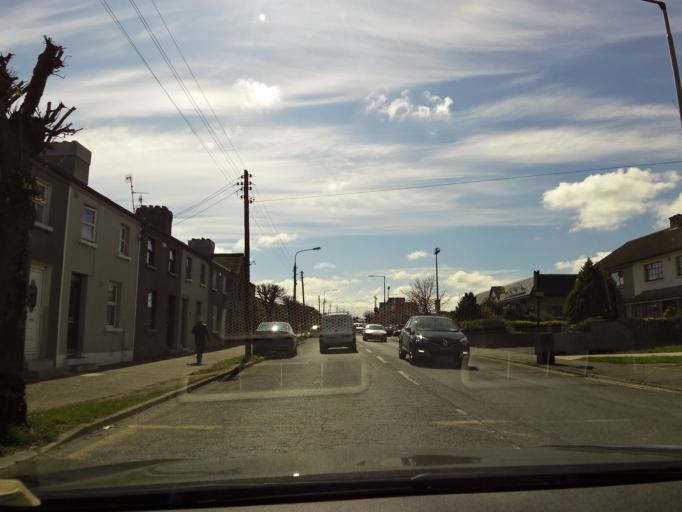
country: IE
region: Leinster
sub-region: Wicklow
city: Arklow
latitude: 52.7939
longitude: -6.1631
